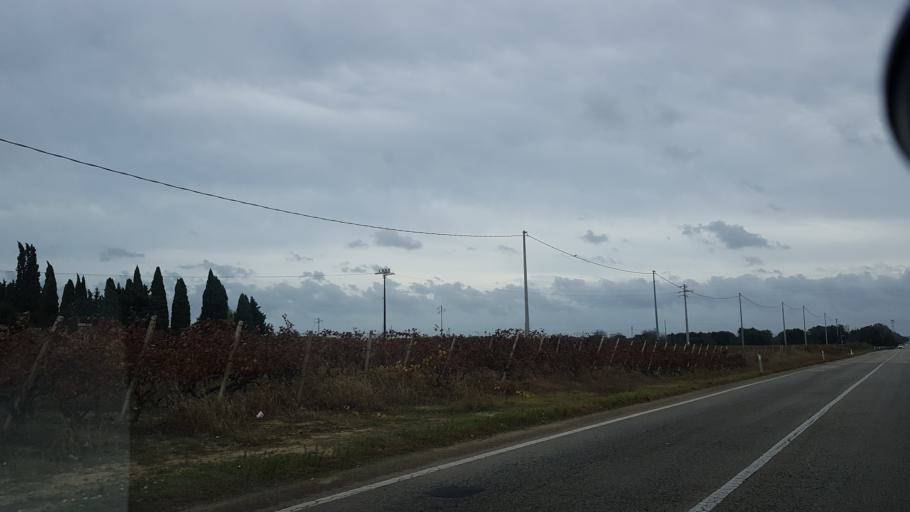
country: IT
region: Apulia
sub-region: Provincia di Lecce
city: Guagnano
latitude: 40.4010
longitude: 17.9603
